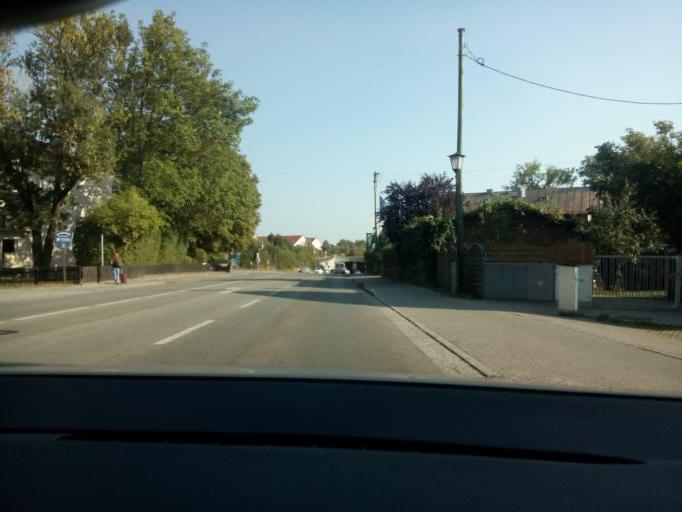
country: DE
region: Bavaria
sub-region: Upper Bavaria
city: Neubiberg
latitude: 48.0797
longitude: 11.6512
